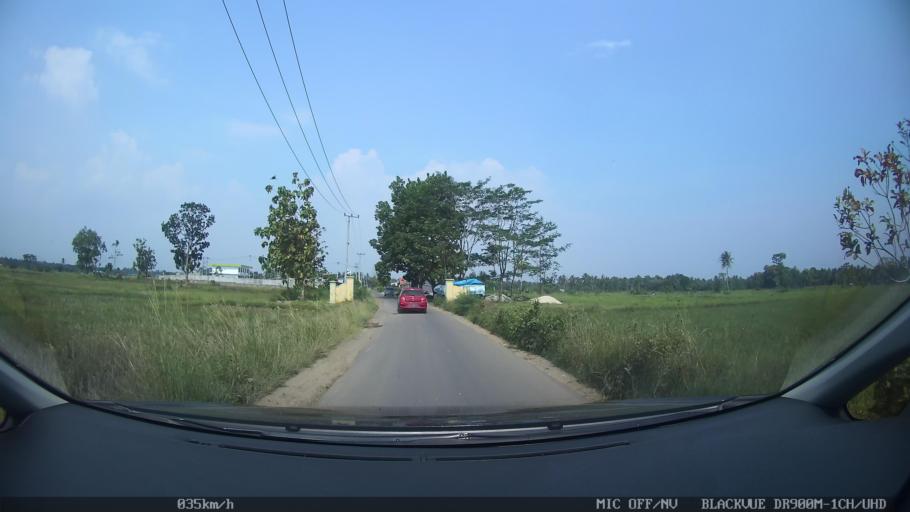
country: ID
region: Lampung
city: Natar
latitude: -5.3060
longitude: 105.2308
